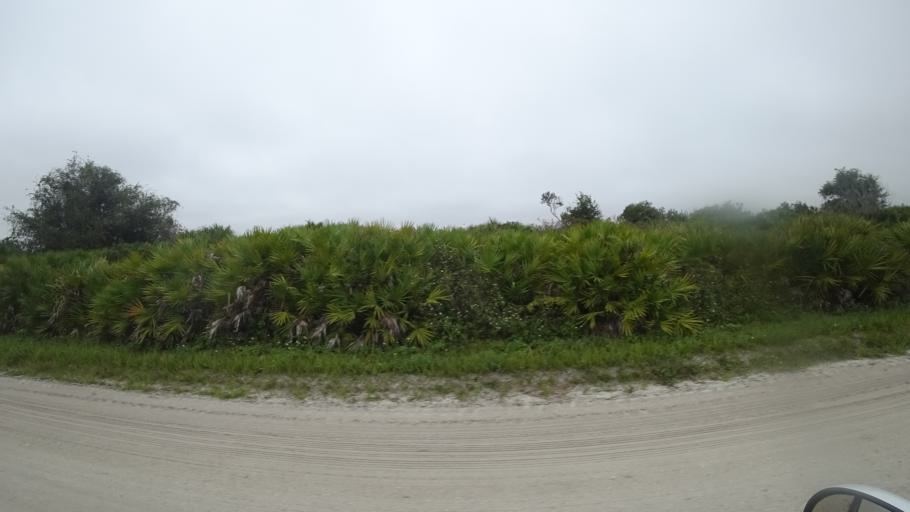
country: US
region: Florida
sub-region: Sarasota County
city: The Meadows
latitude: 27.4512
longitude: -82.3378
